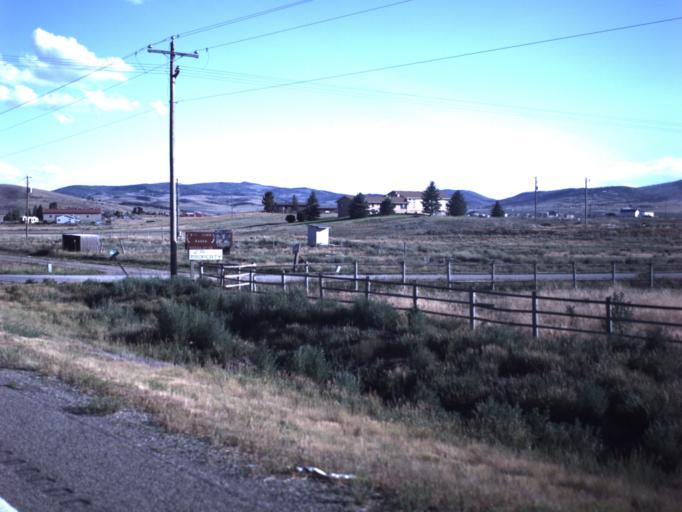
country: US
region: Utah
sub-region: Sanpete County
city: Fairview
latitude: 39.7799
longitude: -111.4917
